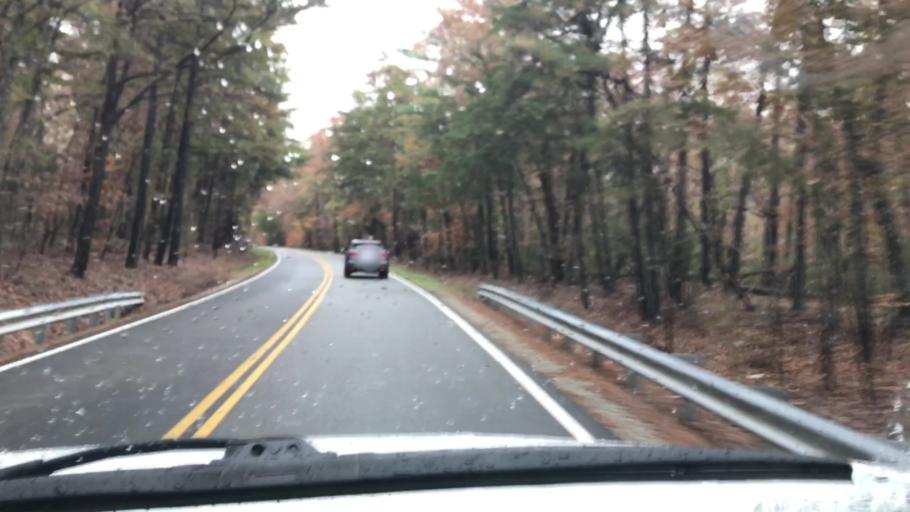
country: US
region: Virginia
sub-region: Henrico County
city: Short Pump
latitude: 37.6121
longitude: -77.6976
